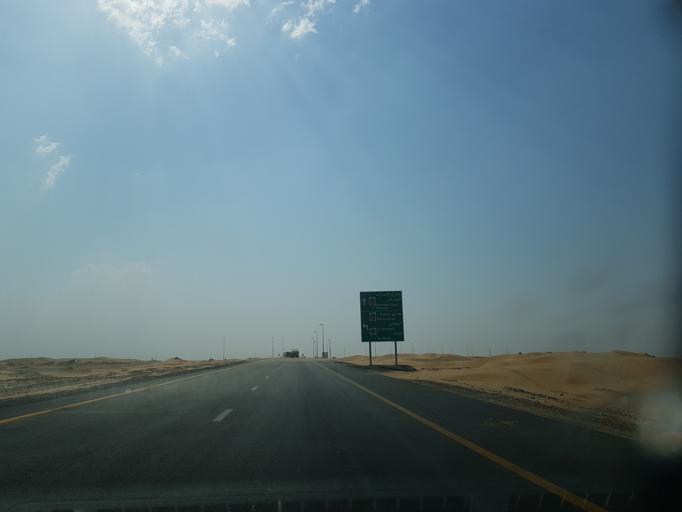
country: AE
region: Ash Shariqah
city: Adh Dhayd
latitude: 25.2676
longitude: 55.6637
